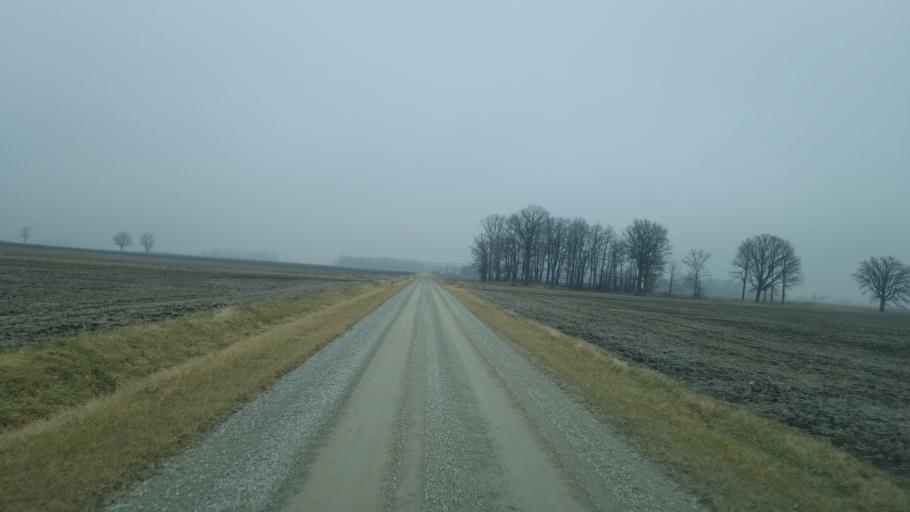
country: US
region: Indiana
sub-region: Adams County
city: Geneva
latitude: 40.6338
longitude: -85.0699
